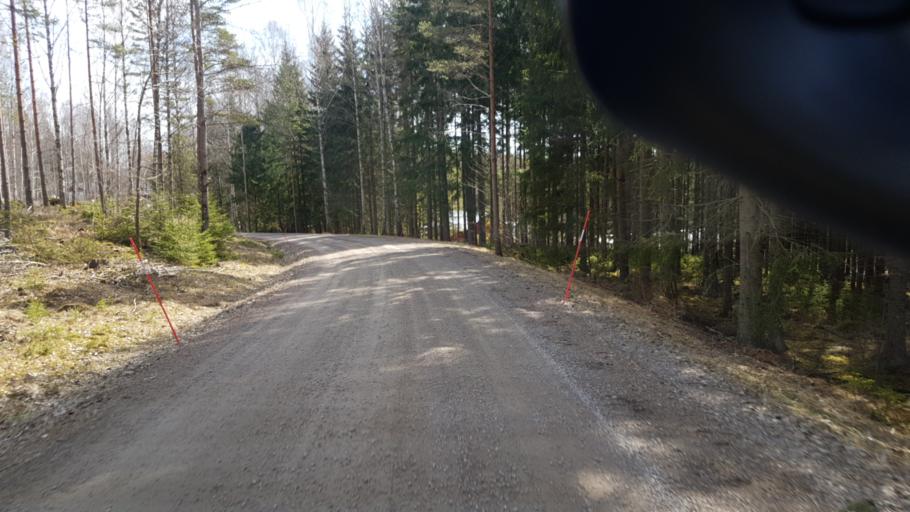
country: SE
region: Vaermland
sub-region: Arvika Kommun
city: Arvika
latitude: 59.5090
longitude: 12.7288
